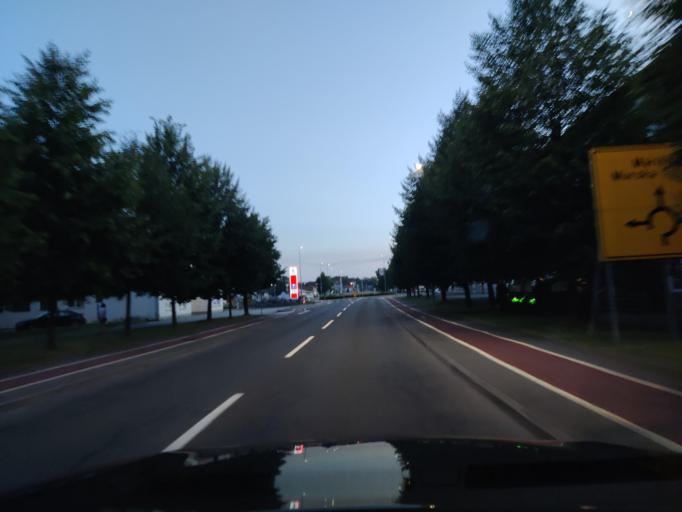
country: SI
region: Lendava-Lendva
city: Lendava
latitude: 46.5619
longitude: 16.4531
